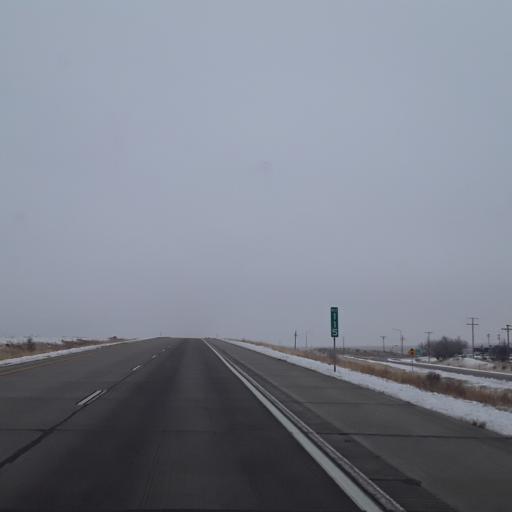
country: US
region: Colorado
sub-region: Logan County
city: Sterling
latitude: 40.4974
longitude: -103.2633
